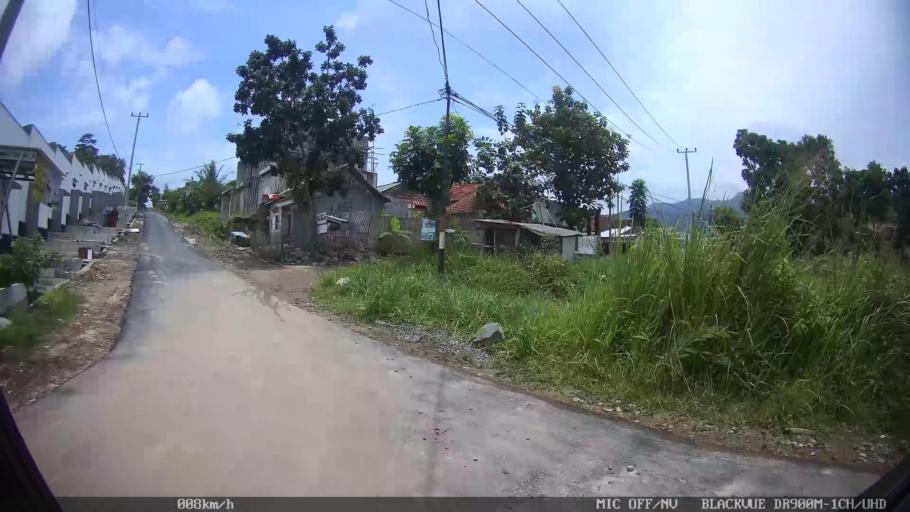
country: ID
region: Lampung
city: Bandarlampung
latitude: -5.4117
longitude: 105.1996
